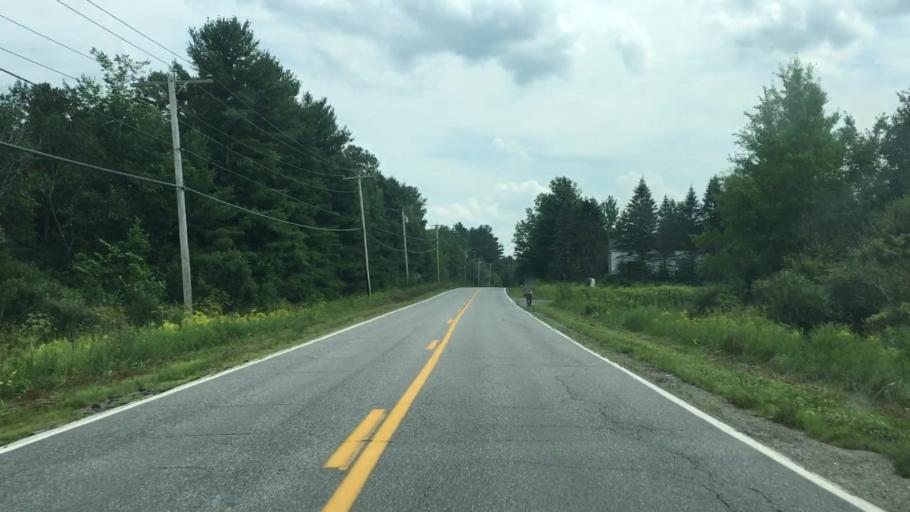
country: US
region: Maine
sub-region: Kennebec County
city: Vassalboro
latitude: 44.4692
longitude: -69.6155
